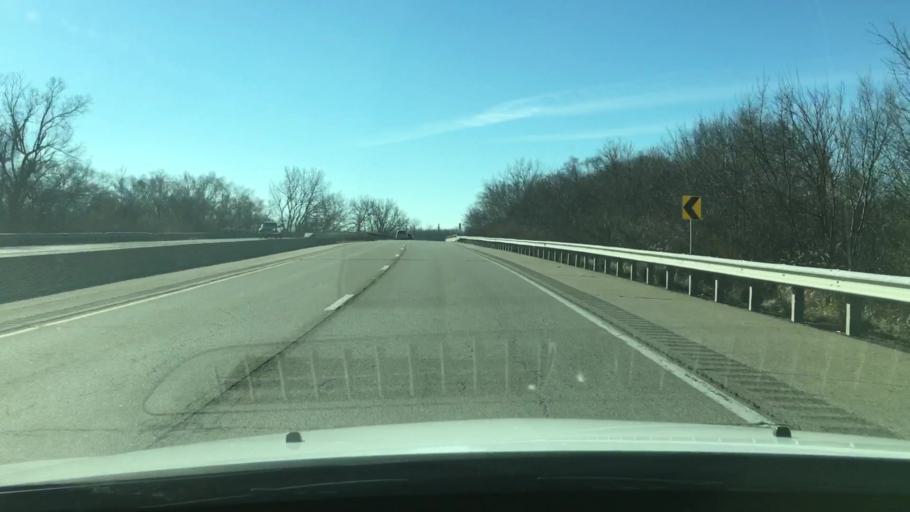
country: US
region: Illinois
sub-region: Tazewell County
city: Pekin
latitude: 40.5716
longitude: -89.7158
